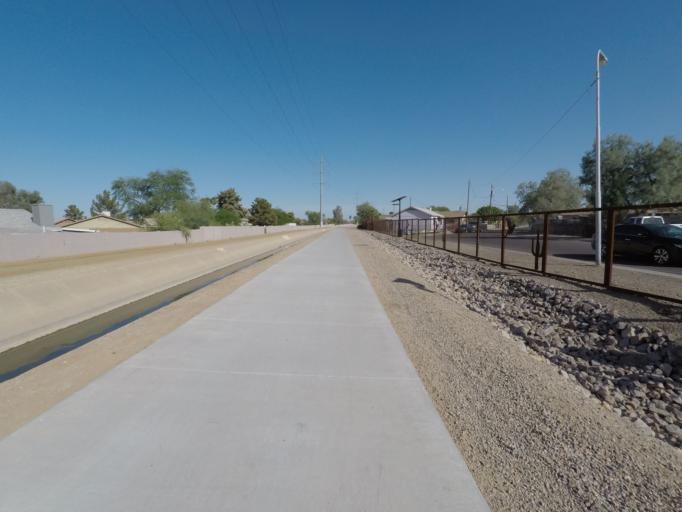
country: US
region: Arizona
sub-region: Maricopa County
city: Guadalupe
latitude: 33.3733
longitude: -111.9609
